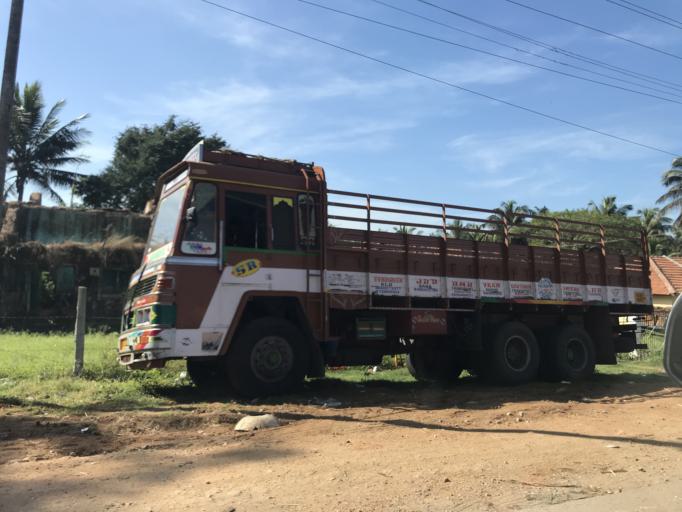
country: IN
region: Karnataka
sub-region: Mysore
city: Sargur
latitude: 12.1217
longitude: 76.4784
